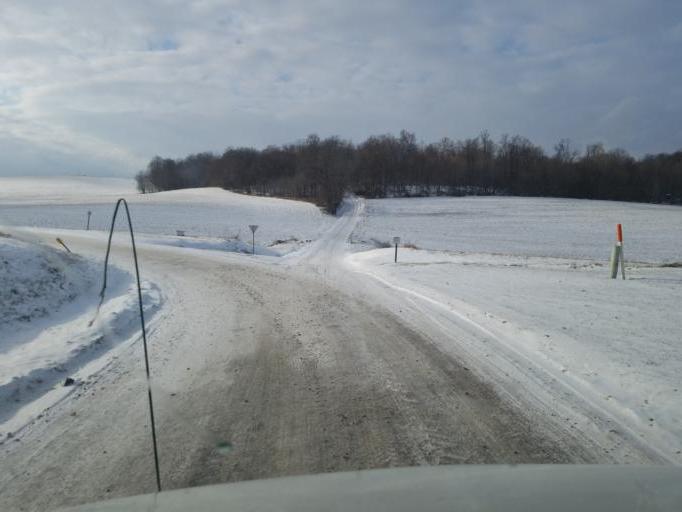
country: US
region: Ohio
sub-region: Holmes County
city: Millersburg
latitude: 40.4691
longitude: -81.9234
